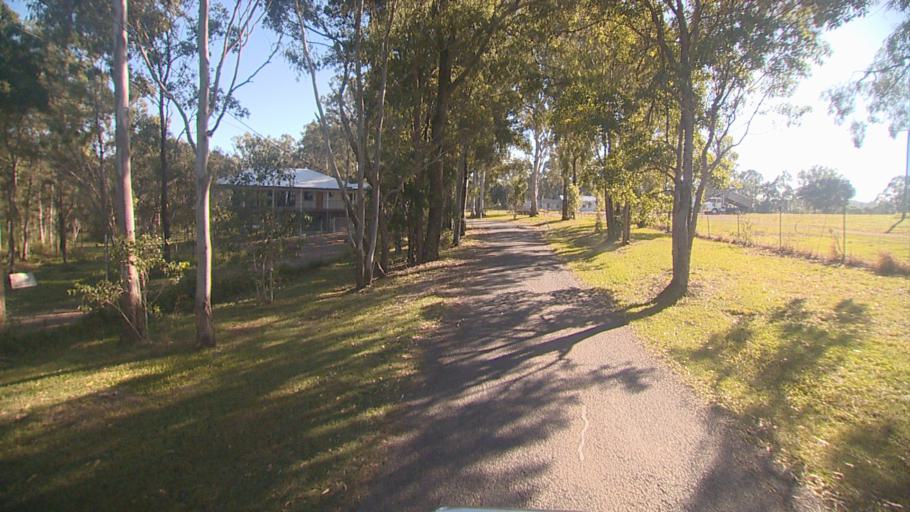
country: AU
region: Queensland
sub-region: Gold Coast
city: Yatala
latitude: -27.6912
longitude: 153.2797
